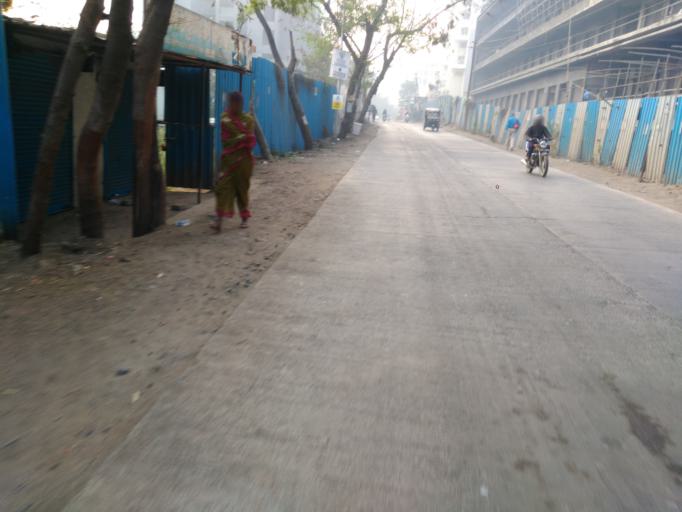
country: IN
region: Maharashtra
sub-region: Pune Division
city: Pune
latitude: 18.4564
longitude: 73.9130
